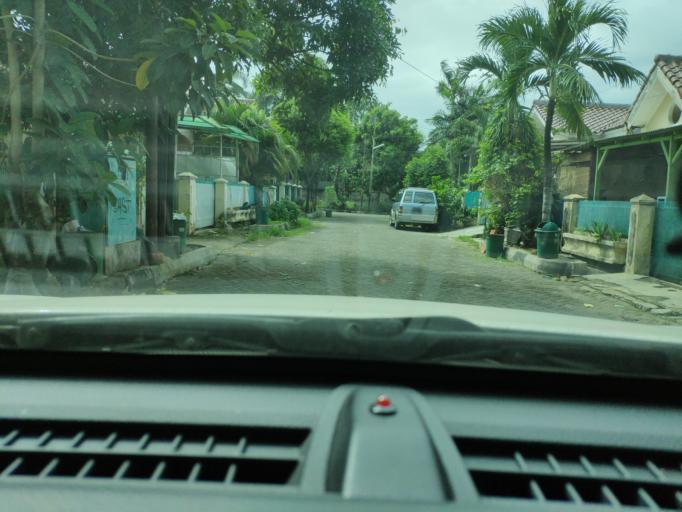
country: ID
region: West Java
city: Ciputat
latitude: -6.2200
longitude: 106.7078
